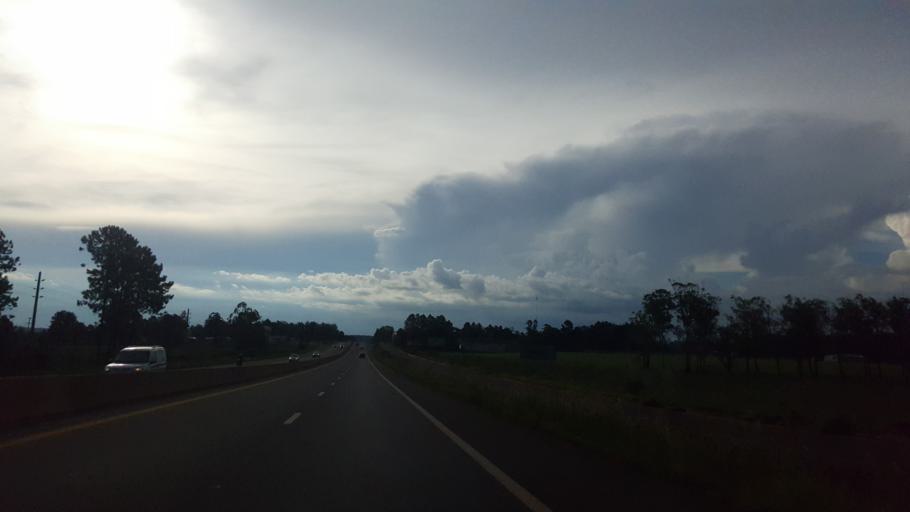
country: AR
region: Misiones
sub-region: Departamento de Candelaria
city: Candelaria
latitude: -27.4689
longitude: -55.7710
